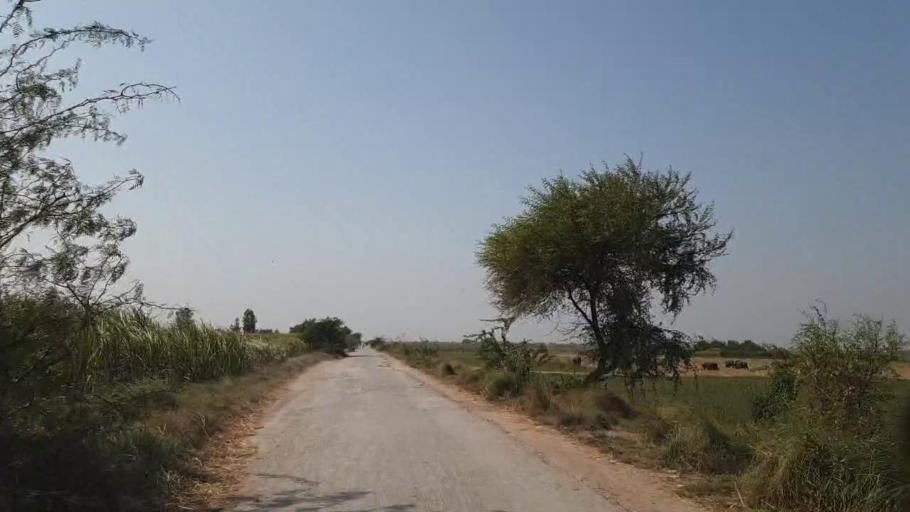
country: PK
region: Sindh
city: Bulri
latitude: 24.9568
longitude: 68.3572
